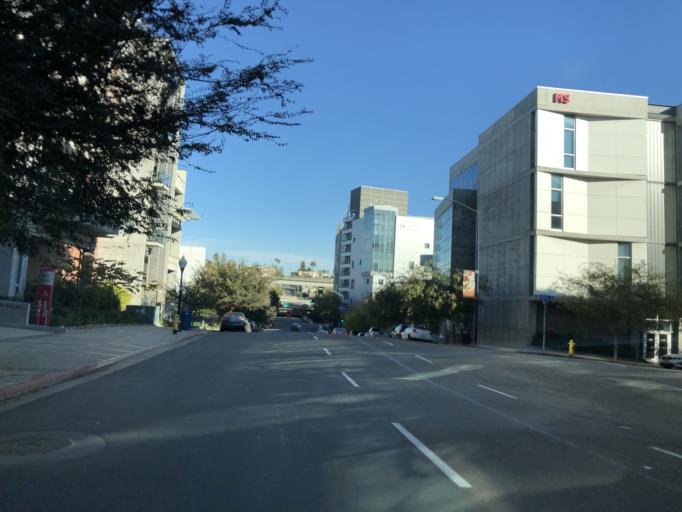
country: US
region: California
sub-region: San Diego County
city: San Diego
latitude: 32.7168
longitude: -117.1508
